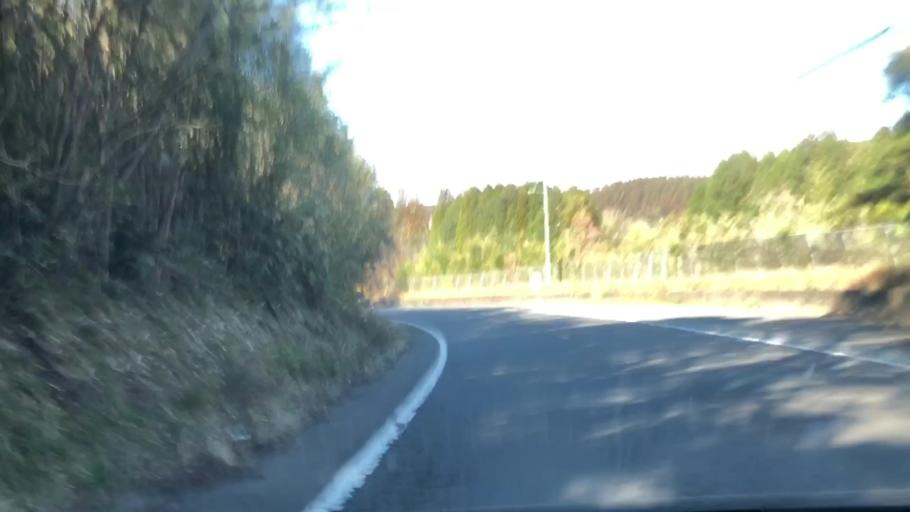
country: JP
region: Kagoshima
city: Satsumasendai
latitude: 31.8417
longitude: 130.4298
